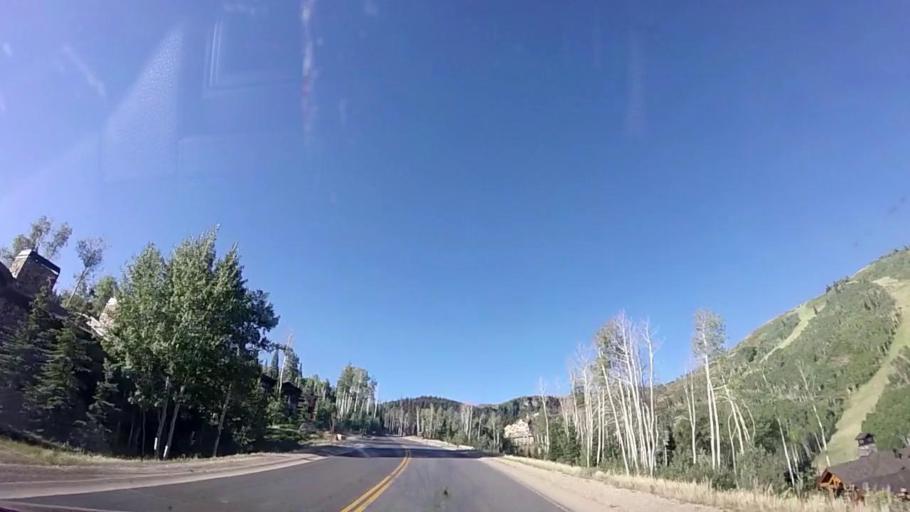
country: US
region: Utah
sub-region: Summit County
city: Park City
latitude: 40.6207
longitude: -111.5069
